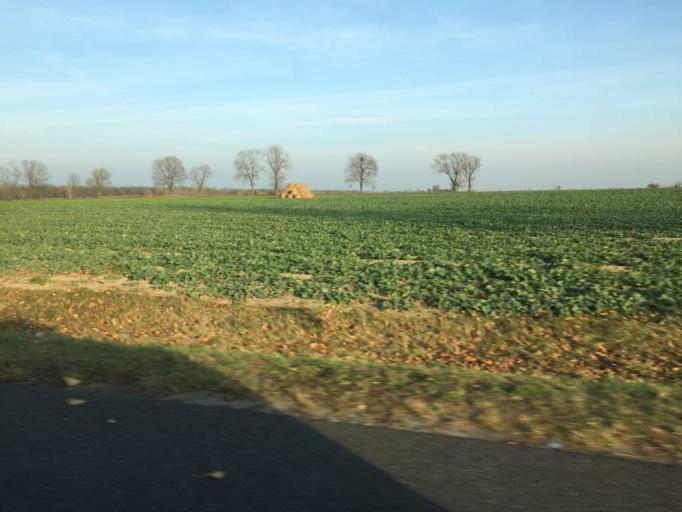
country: PL
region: Opole Voivodeship
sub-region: Powiat strzelecki
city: Strzelce Opolskie
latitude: 50.4966
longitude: 18.3373
